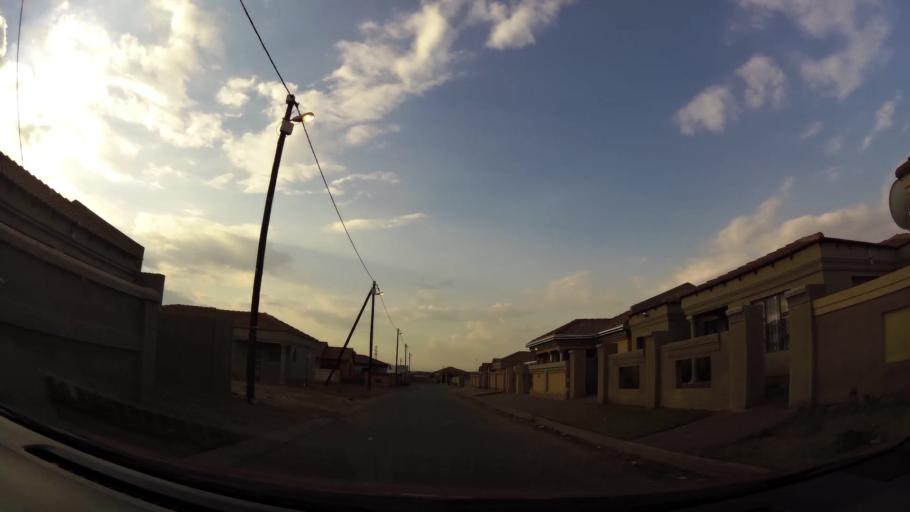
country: ZA
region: Gauteng
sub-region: Sedibeng District Municipality
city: Vanderbijlpark
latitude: -26.6086
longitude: 27.8121
